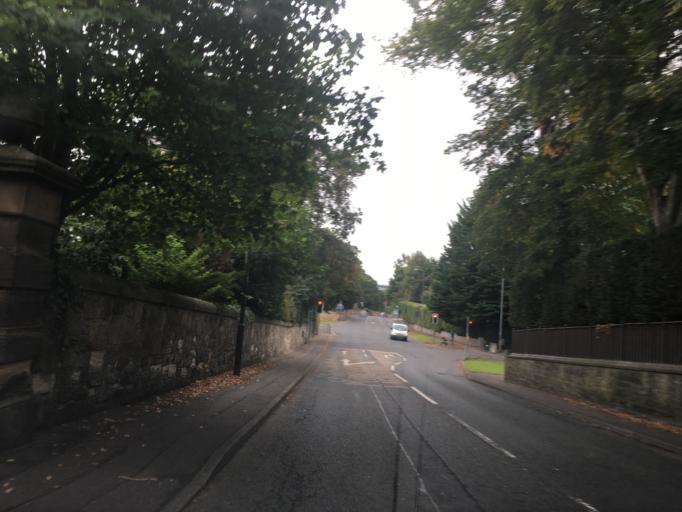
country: GB
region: Scotland
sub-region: Midlothian
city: Dalkeith
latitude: 55.8870
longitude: -3.0759
